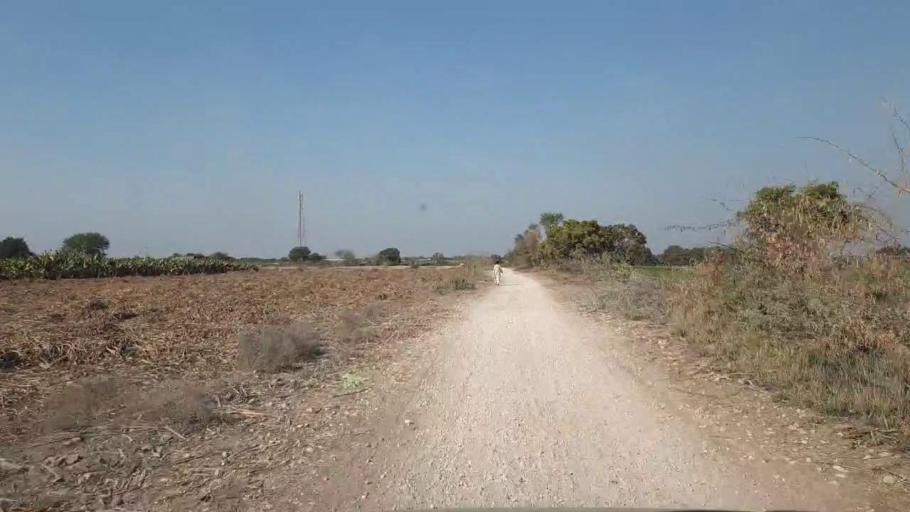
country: PK
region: Sindh
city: Chambar
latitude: 25.3190
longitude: 68.7597
